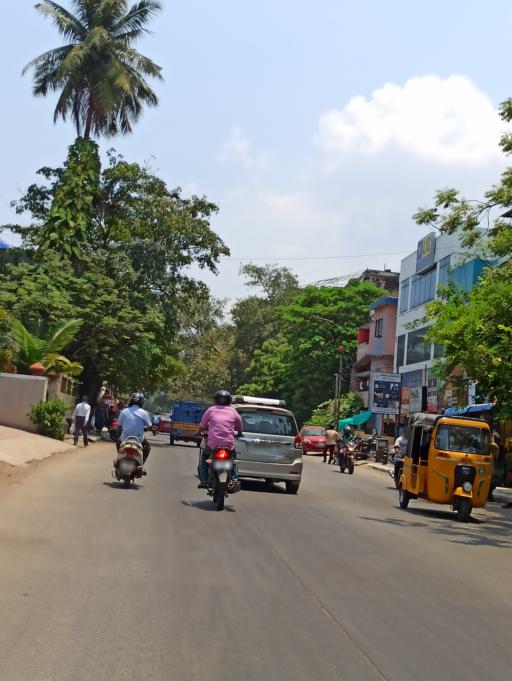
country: IN
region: Tamil Nadu
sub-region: Chennai
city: Chetput
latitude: 13.0859
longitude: 80.2344
